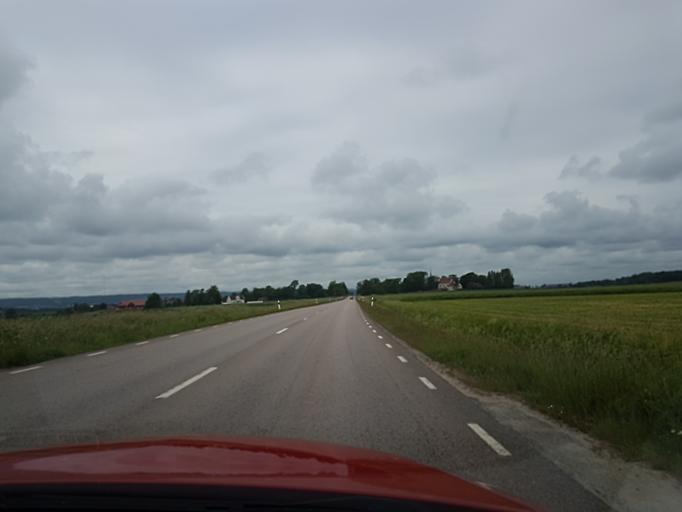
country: SE
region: Vaestra Goetaland
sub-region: Skovde Kommun
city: Skoevde
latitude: 58.3852
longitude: 13.9430
